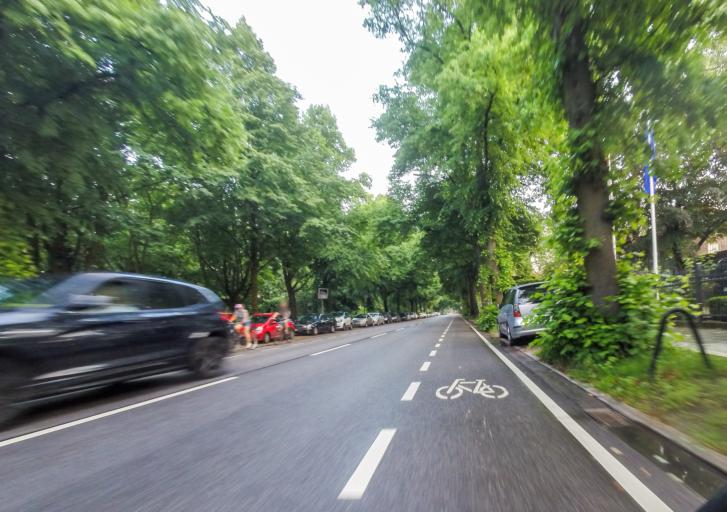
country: DE
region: Hamburg
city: Winterhude
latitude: 53.5976
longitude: 9.9941
